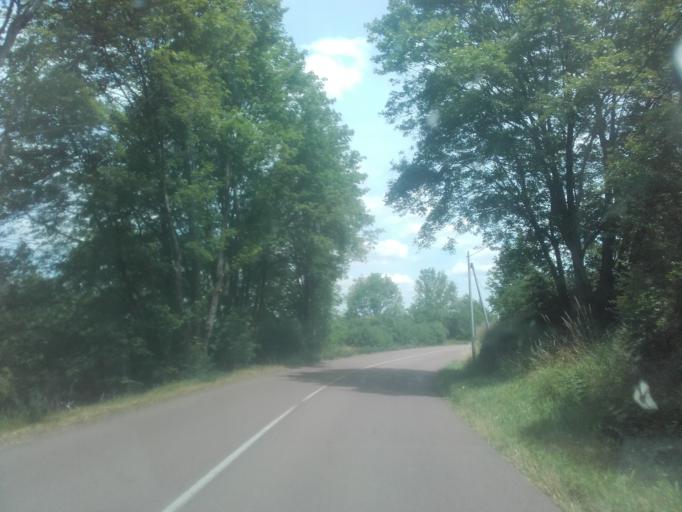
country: FR
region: Bourgogne
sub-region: Departement de Saone-et-Loire
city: Rully
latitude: 46.9037
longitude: 4.6967
